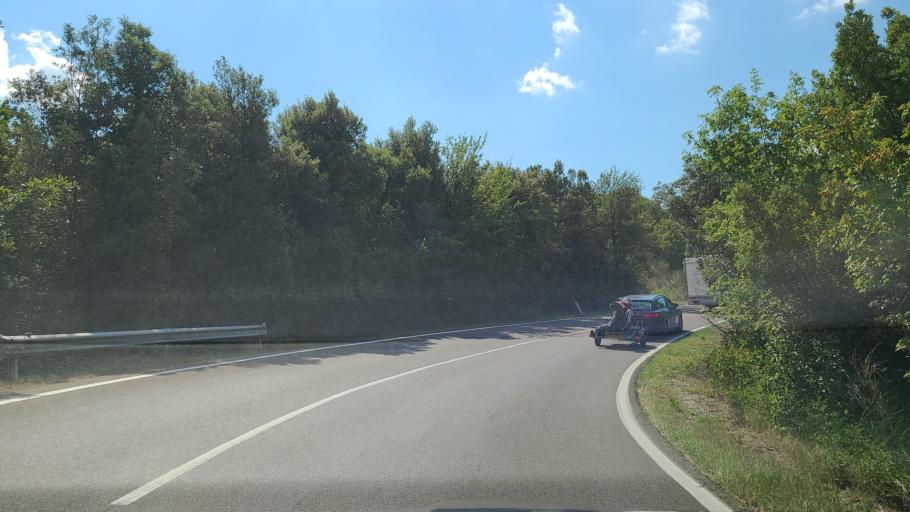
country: IT
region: Tuscany
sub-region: Provincia di Siena
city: Casole d'Elsa
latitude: 43.4015
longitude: 10.9987
